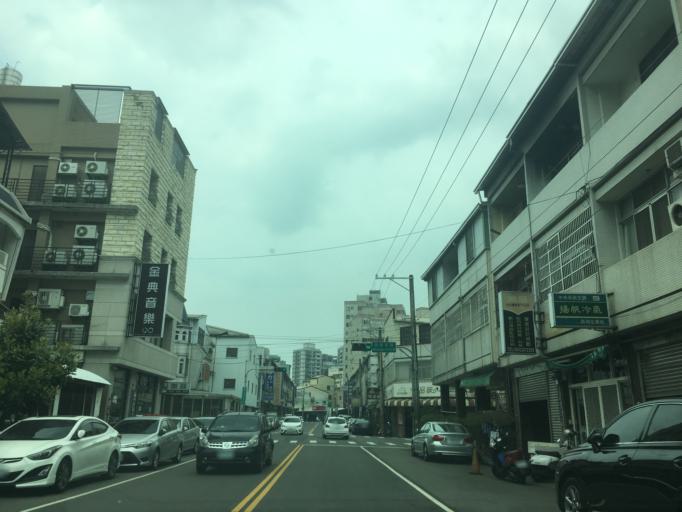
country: TW
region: Taiwan
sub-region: Taichung City
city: Taichung
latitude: 24.1785
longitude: 120.6885
